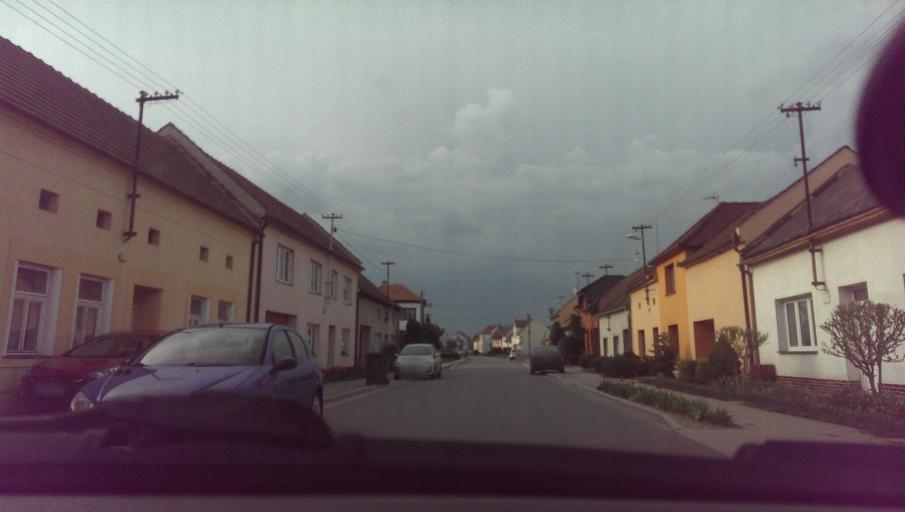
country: CZ
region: Zlin
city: Knezpole
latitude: 49.0975
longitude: 17.5173
